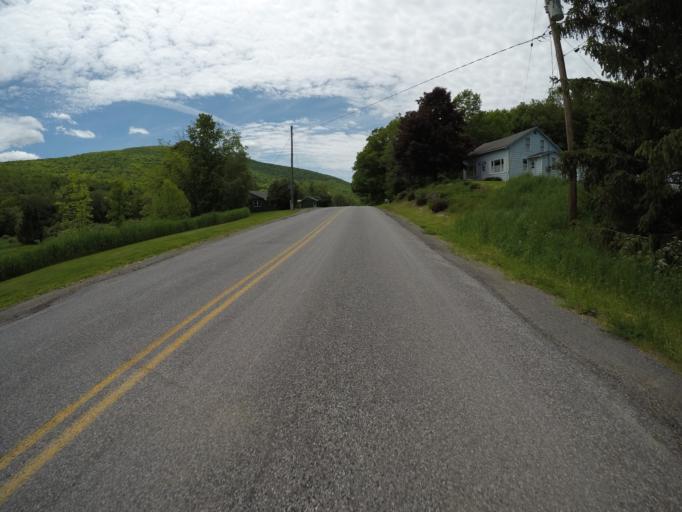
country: US
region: New York
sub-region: Delaware County
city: Stamford
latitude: 42.2485
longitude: -74.5369
